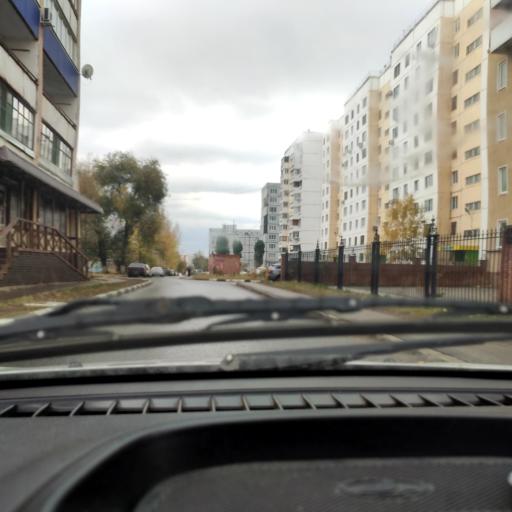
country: RU
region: Samara
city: Zhigulevsk
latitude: 53.4812
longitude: 49.4814
